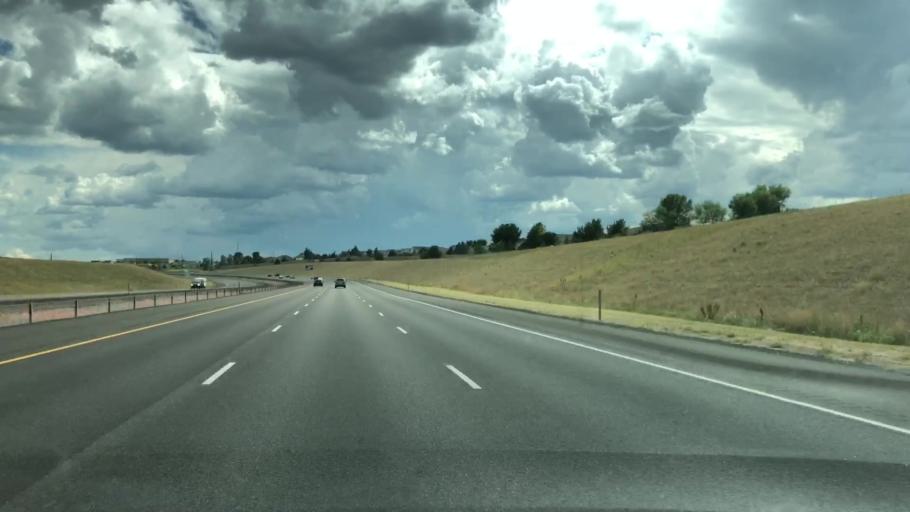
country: US
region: Colorado
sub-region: Douglas County
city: Parker
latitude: 39.6219
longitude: -104.7184
